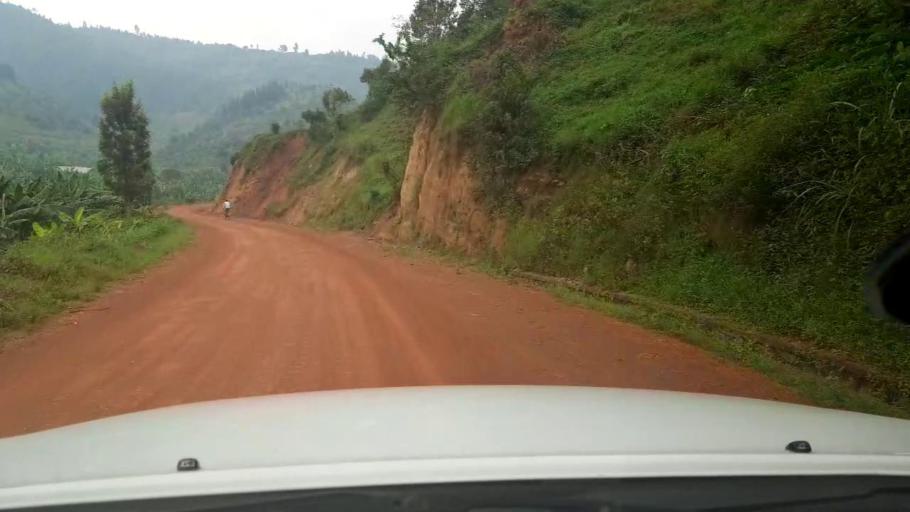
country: RW
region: Kigali
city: Kigali
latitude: -1.8524
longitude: 29.9038
